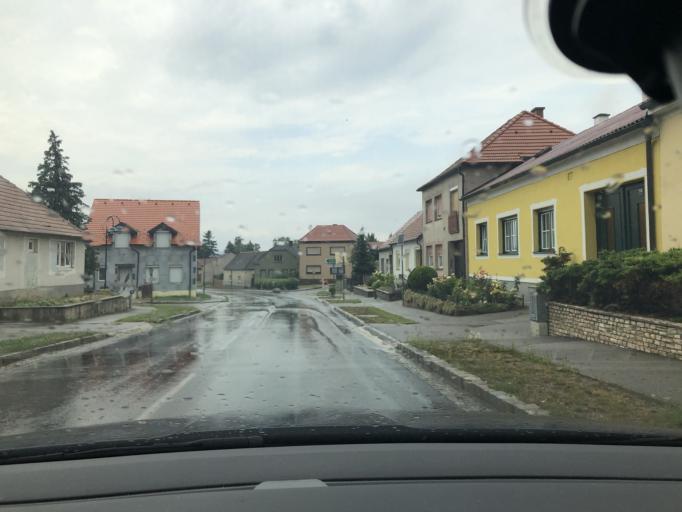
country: AT
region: Lower Austria
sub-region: Politischer Bezirk Ganserndorf
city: Gross-Schweinbarth
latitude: 48.3951
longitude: 16.6565
